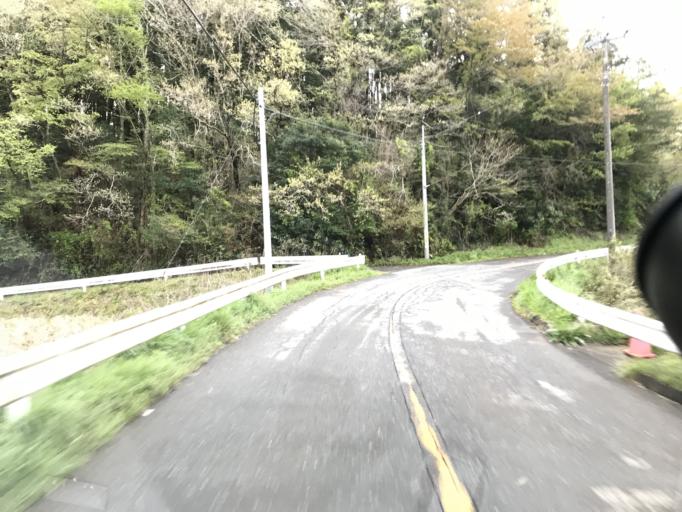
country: JP
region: Chiba
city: Sawara
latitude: 35.7753
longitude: 140.4526
